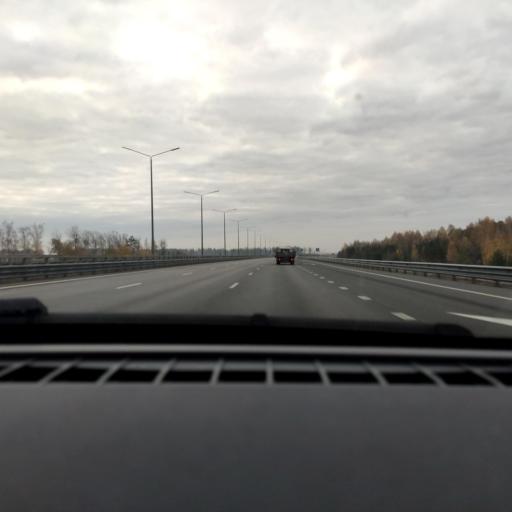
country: RU
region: Voronezj
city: Somovo
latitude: 51.7855
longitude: 39.2860
